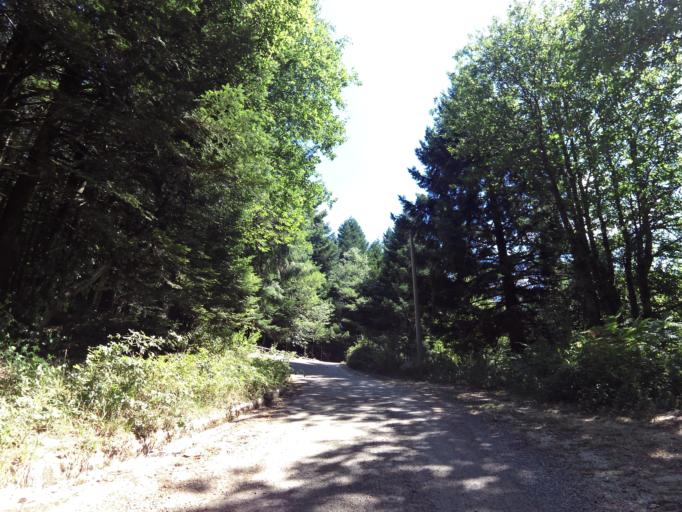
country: IT
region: Calabria
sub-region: Provincia di Vibo-Valentia
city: Serra San Bruno
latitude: 38.5581
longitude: 16.3324
